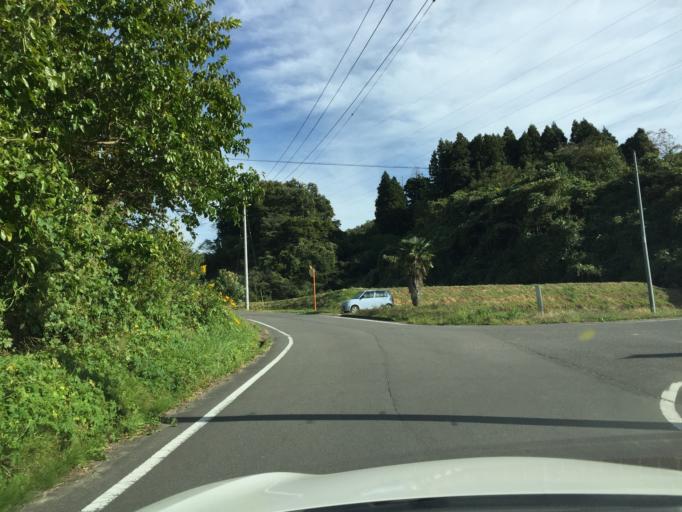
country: JP
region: Fukushima
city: Miharu
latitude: 37.3521
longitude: 140.4888
